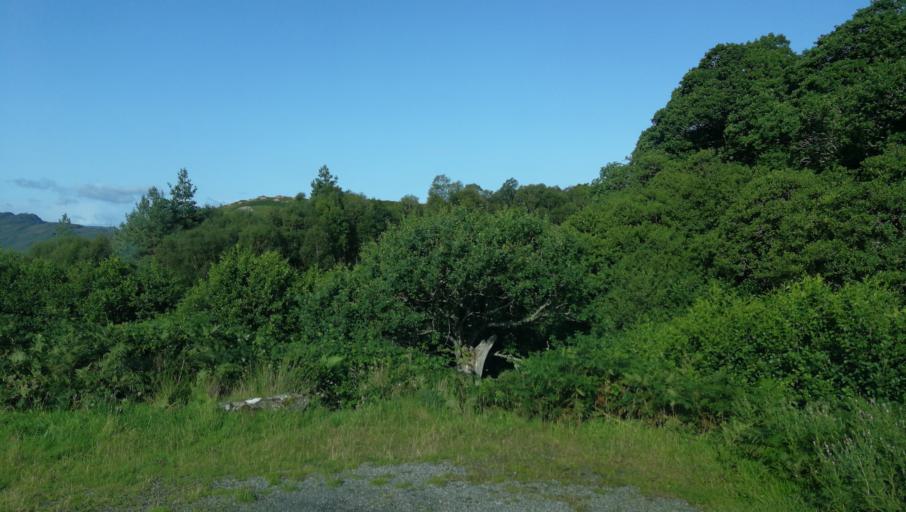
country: GB
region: Scotland
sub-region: Argyll and Bute
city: Isle Of Mull
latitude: 56.6784
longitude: -5.8385
